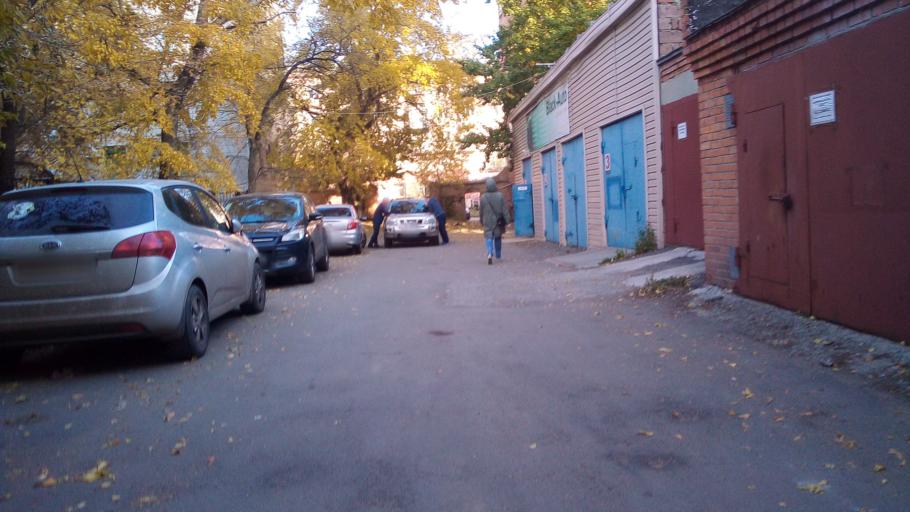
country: RU
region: Chelyabinsk
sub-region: Gorod Chelyabinsk
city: Chelyabinsk
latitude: 55.1520
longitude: 61.4114
